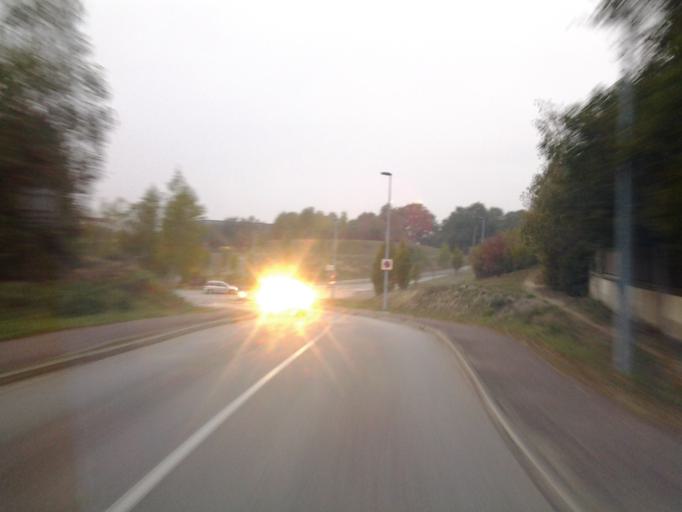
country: FR
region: Pays de la Loire
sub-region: Departement de la Vendee
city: La Roche-sur-Yon
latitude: 46.6457
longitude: -1.4316
